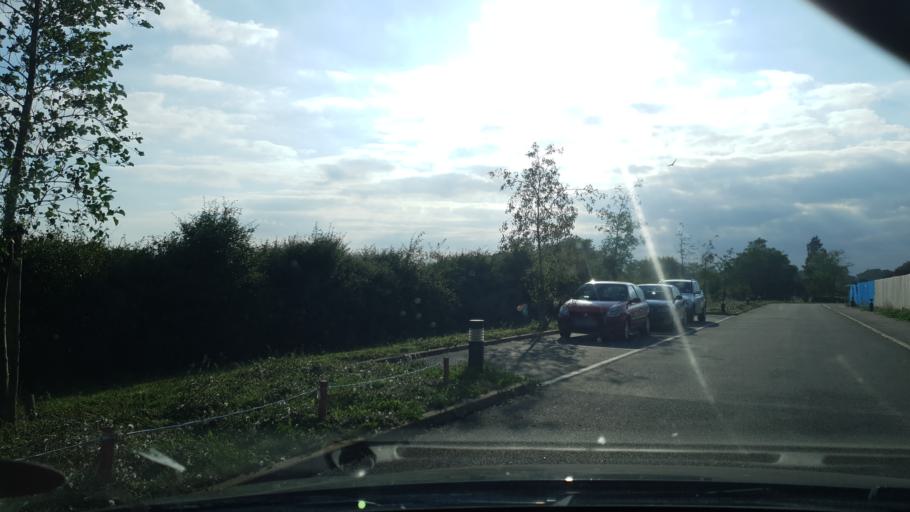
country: GB
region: England
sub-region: Essex
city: Frinton-on-Sea
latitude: 51.8394
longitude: 1.2201
